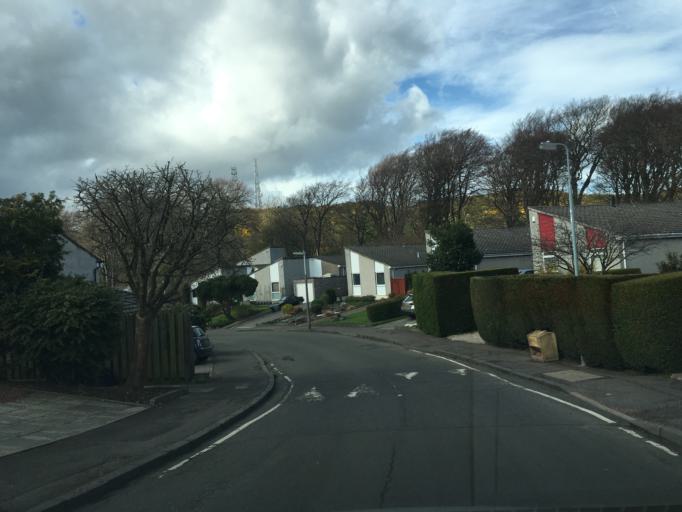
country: GB
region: Scotland
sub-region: Edinburgh
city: Edinburgh
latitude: 55.9085
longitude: -3.1990
